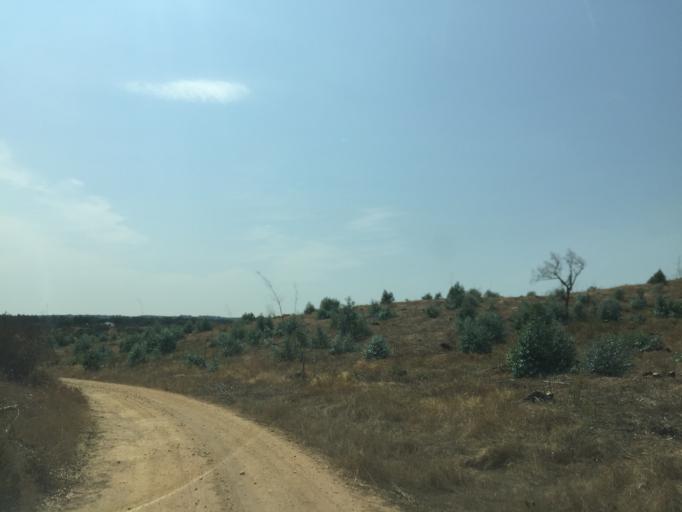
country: PT
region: Setubal
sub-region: Grandola
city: Grandola
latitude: 38.0475
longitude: -8.4685
